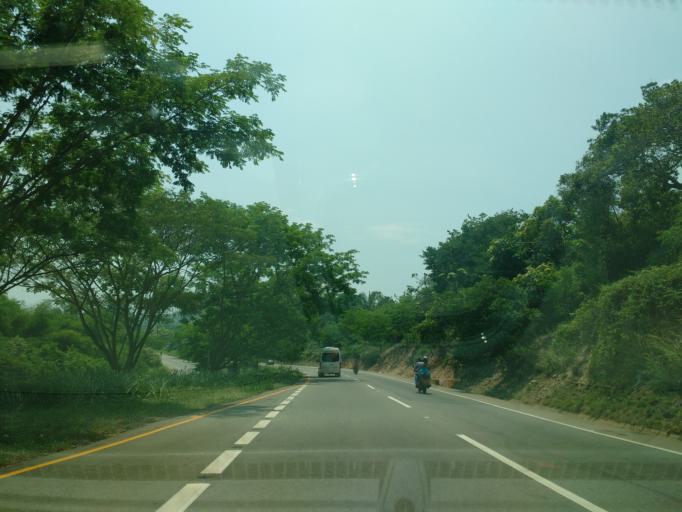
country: CO
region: Tolima
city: Melgar
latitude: 4.2174
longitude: -74.6603
